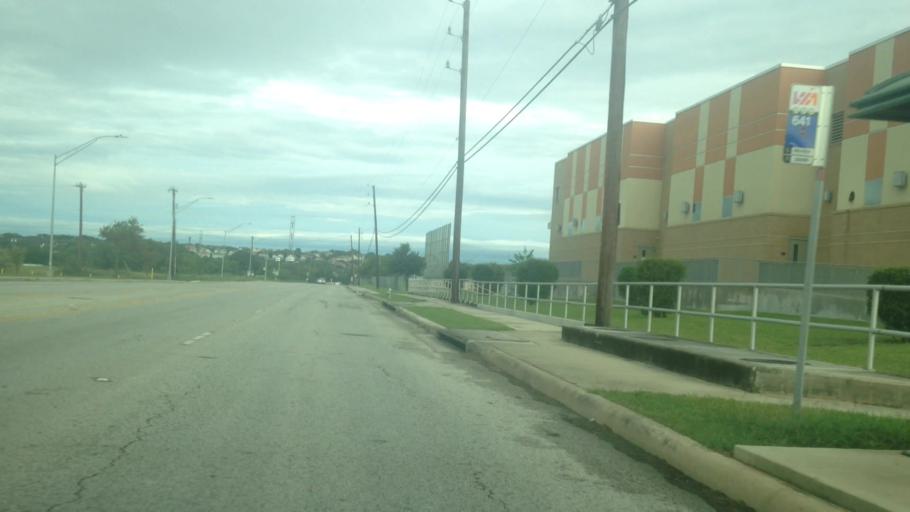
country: US
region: Texas
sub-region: Bexar County
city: Live Oak
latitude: 29.5814
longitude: -98.3930
